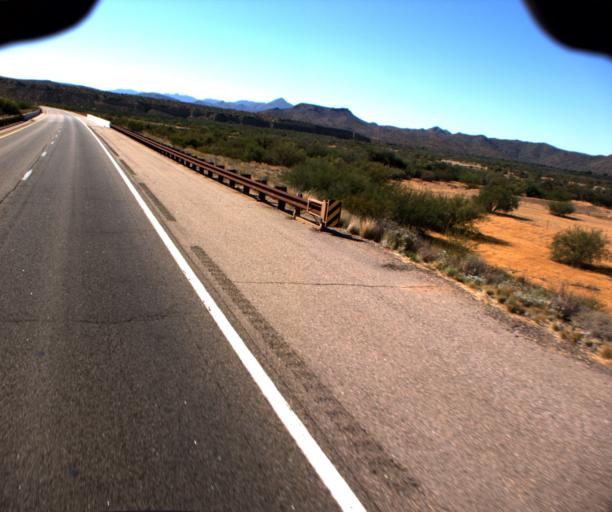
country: US
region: Arizona
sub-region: Yavapai County
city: Bagdad
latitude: 34.6448
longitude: -113.5676
